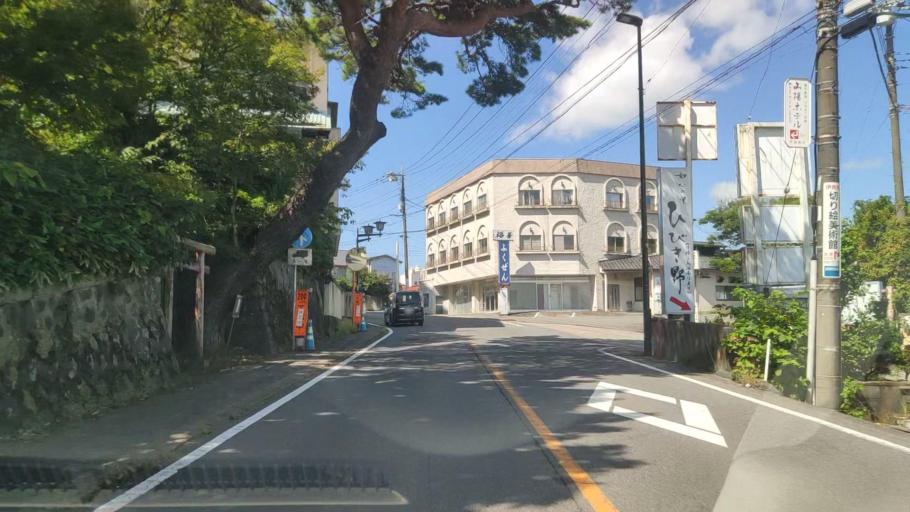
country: JP
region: Gunma
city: Shibukawa
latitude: 36.4999
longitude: 138.9255
